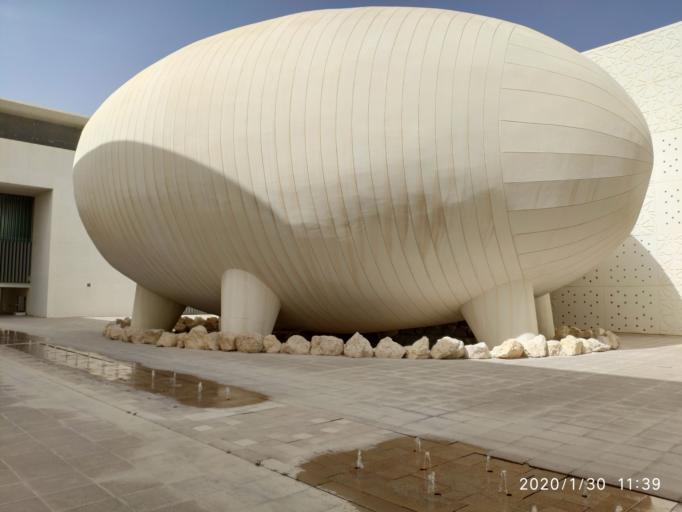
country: QA
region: Baladiyat ar Rayyan
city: Ar Rayyan
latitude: 25.3180
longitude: 51.4394
